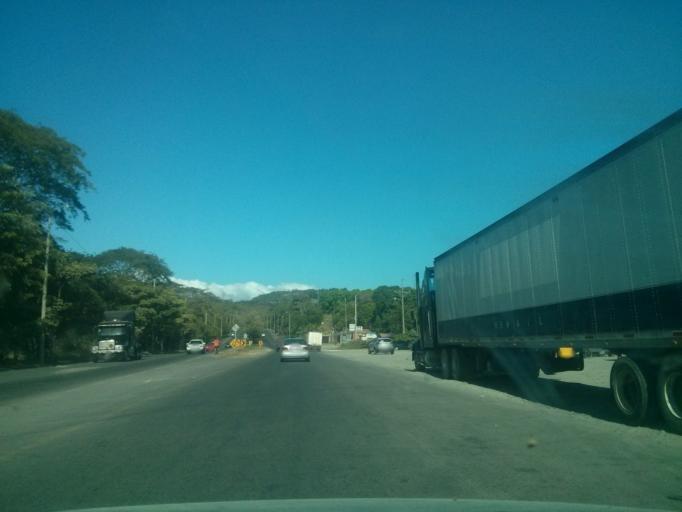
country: CR
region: Puntarenas
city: Esparza
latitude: 9.9927
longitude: -84.7203
